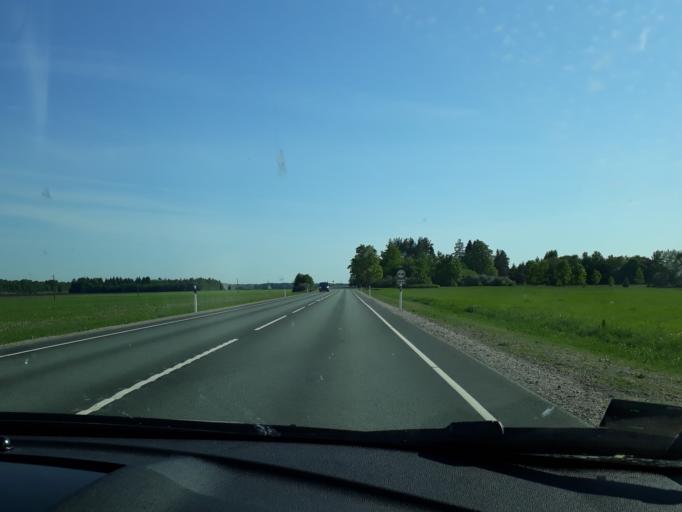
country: EE
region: Paernumaa
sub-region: Tootsi vald
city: Tootsi
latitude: 58.5478
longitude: 24.8479
